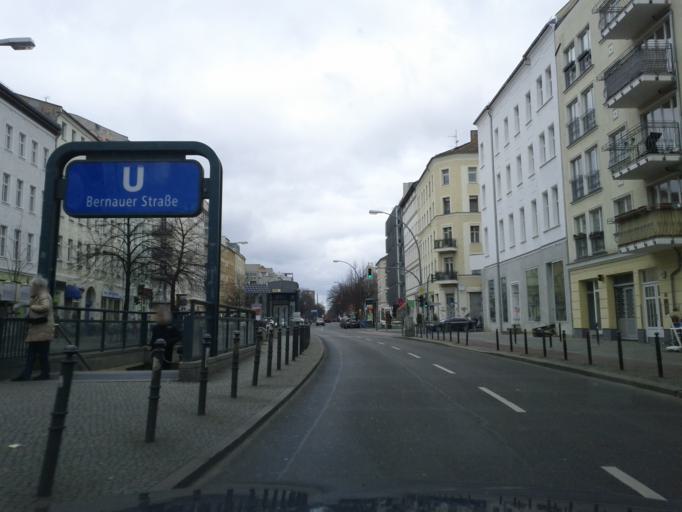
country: DE
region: Berlin
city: Gesundbrunnen
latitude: 52.5365
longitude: 13.3974
